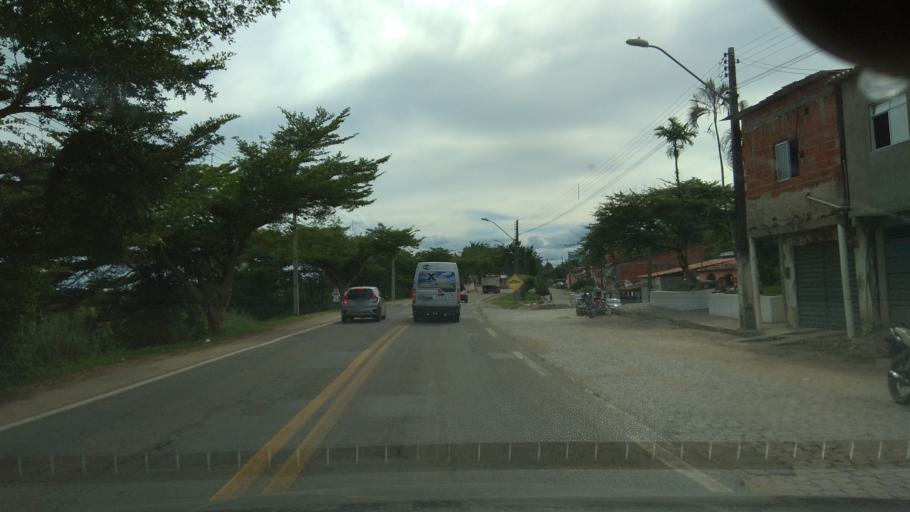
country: BR
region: Bahia
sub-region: Ubata
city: Ubata
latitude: -14.2077
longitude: -39.6017
